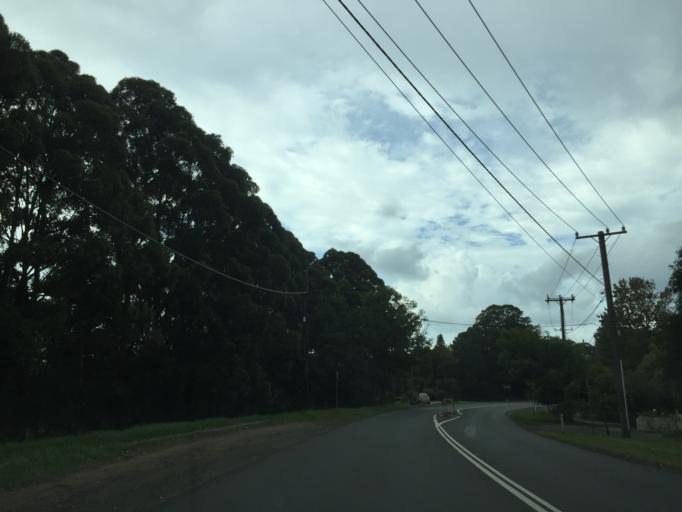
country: AU
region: New South Wales
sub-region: Hornsby Shire
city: Galston
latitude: -33.6534
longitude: 151.0542
